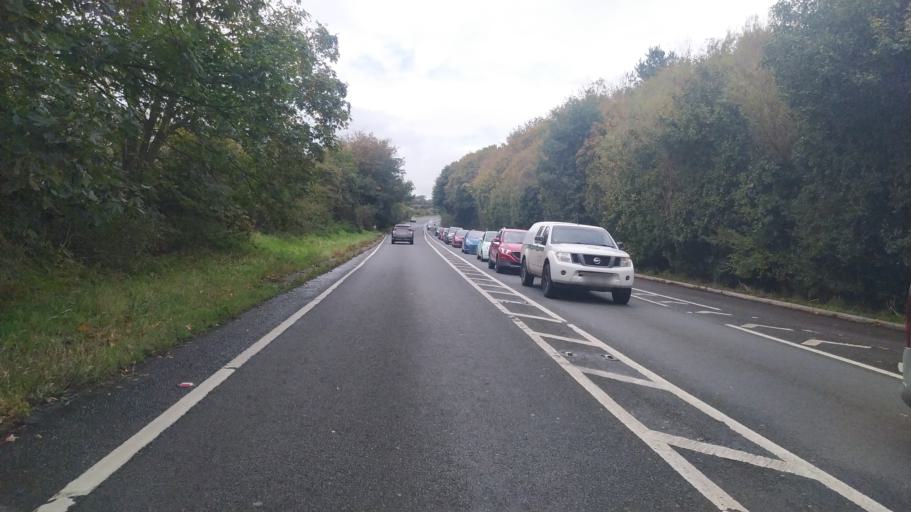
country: GB
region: England
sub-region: Dorset
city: Bridport
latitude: 50.7233
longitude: -2.7667
